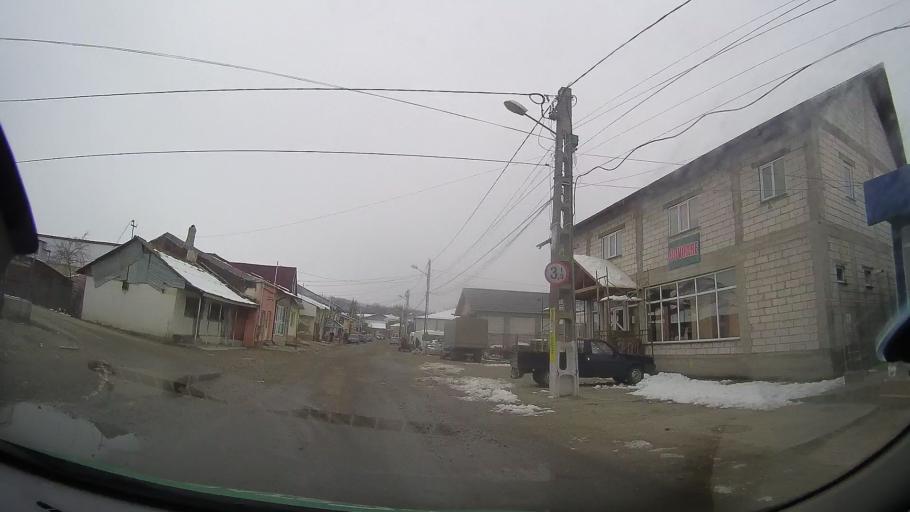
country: RO
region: Bacau
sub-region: Comuna Podu Turcului
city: Podu Turcului
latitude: 46.2048
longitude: 27.3837
